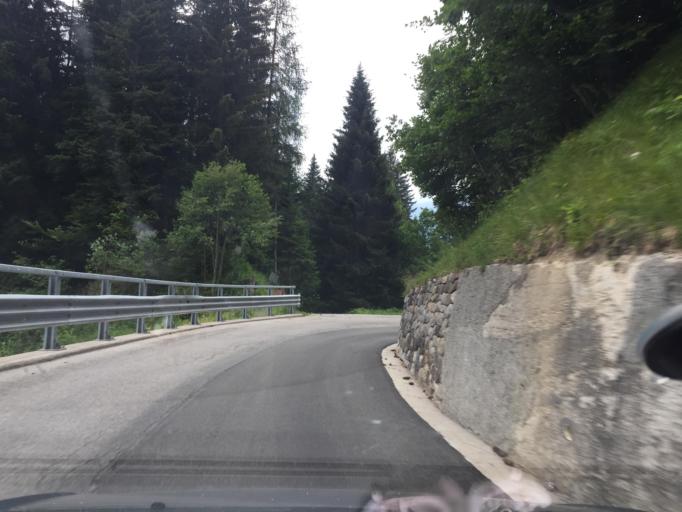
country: IT
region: Friuli Venezia Giulia
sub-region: Provincia di Udine
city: Rigolato
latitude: 46.5814
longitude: 12.8242
